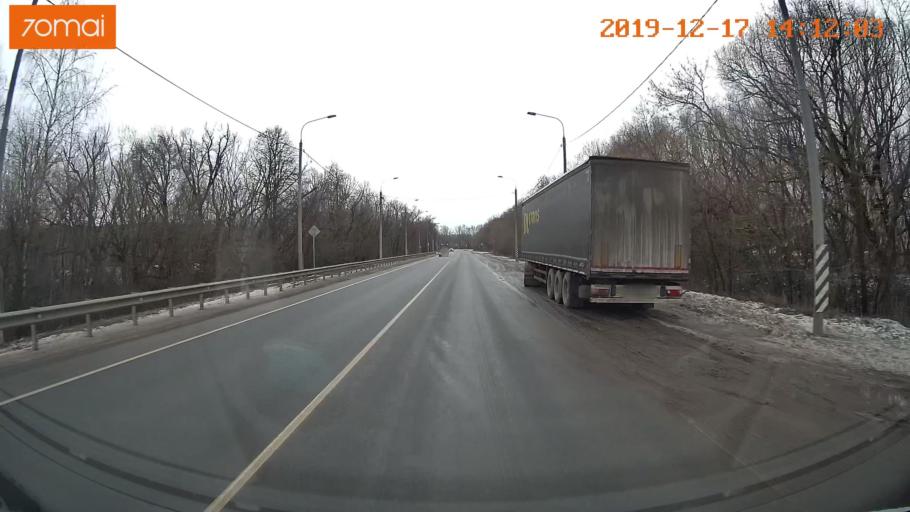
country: RU
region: Rjazan
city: Rybnoye
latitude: 54.5274
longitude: 39.5072
